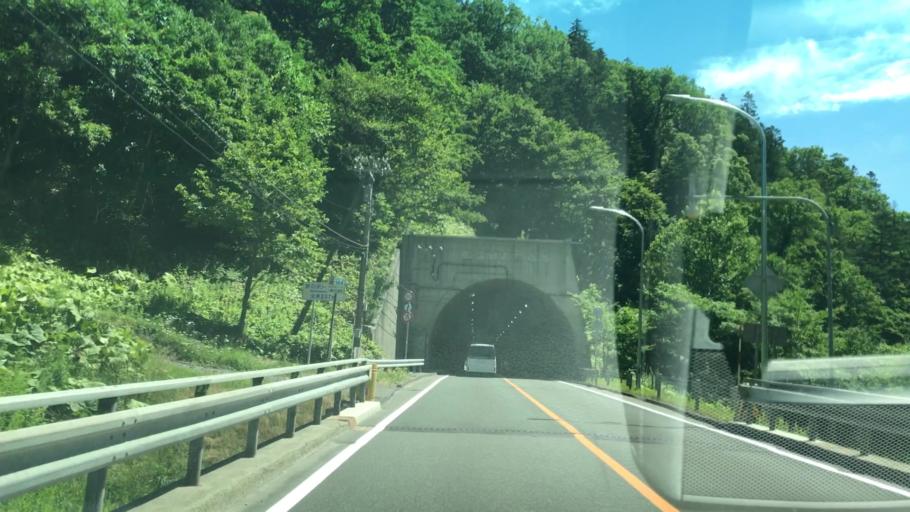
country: JP
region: Hokkaido
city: Shimo-furano
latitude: 42.9639
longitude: 142.6415
